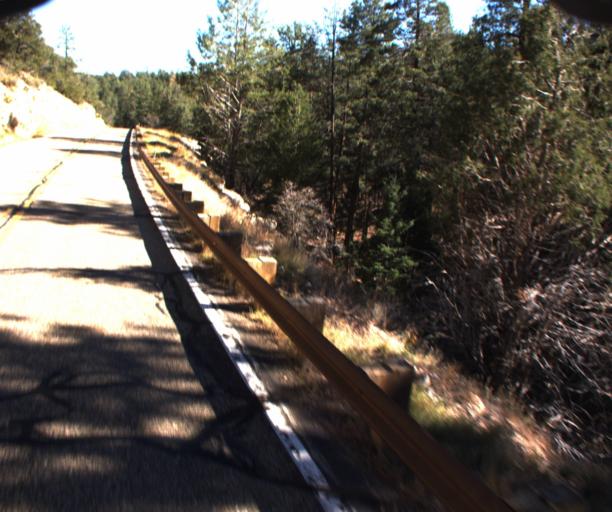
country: US
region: Arizona
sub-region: Coconino County
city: Fredonia
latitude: 36.7335
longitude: -112.1649
